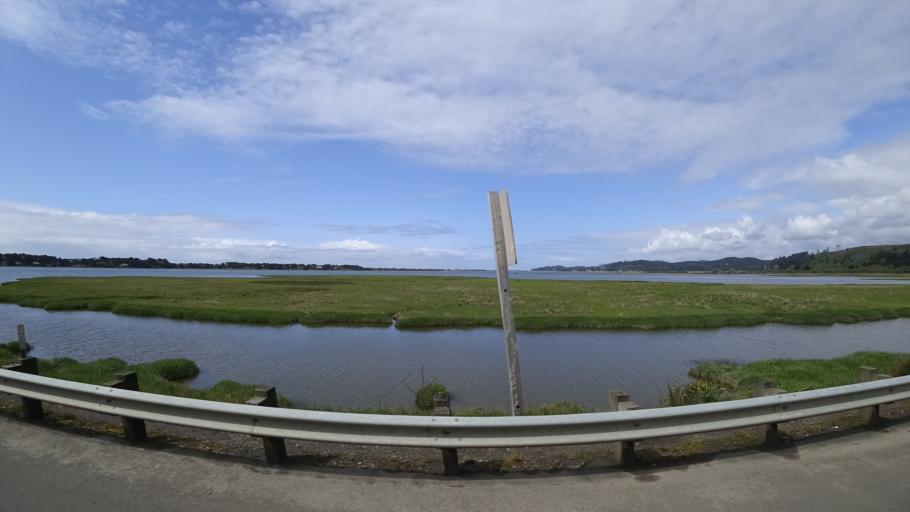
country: US
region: Oregon
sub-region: Lincoln County
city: Lincoln Beach
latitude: 44.8935
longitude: -124.0168
